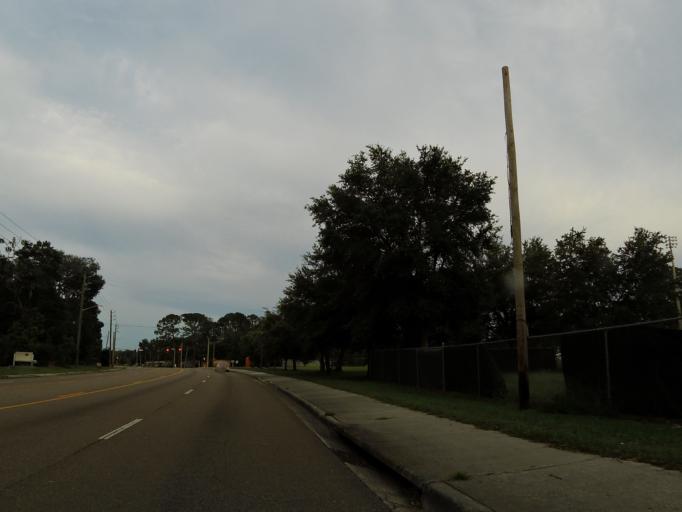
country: US
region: Florida
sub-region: Duval County
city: Jacksonville
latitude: 30.3837
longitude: -81.7074
